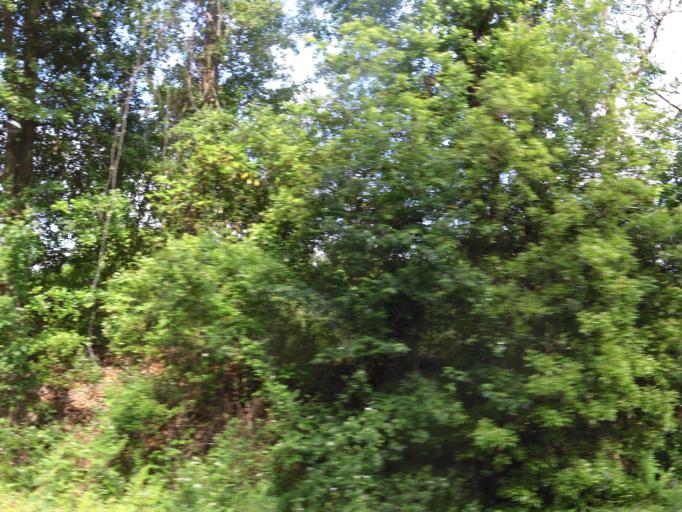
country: US
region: Georgia
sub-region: Charlton County
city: Folkston
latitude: 30.8178
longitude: -82.0707
